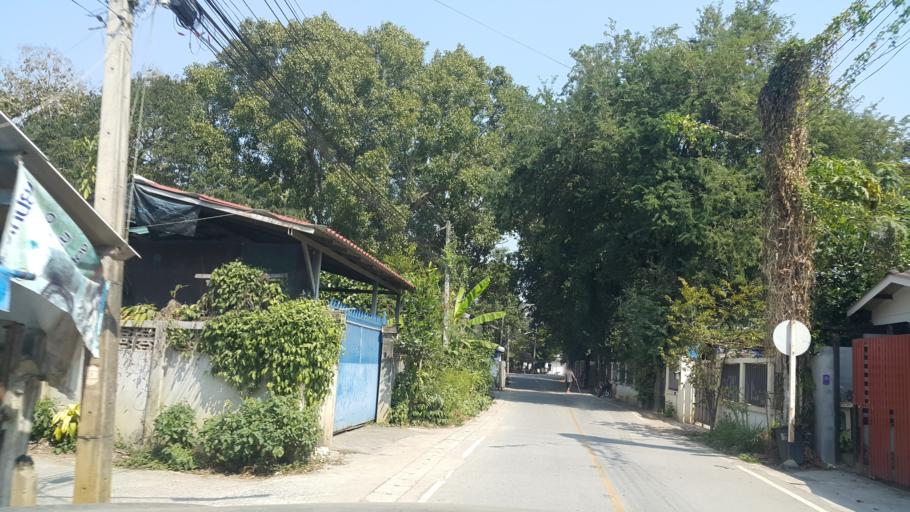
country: TH
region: Chiang Mai
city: Chiang Mai
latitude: 18.7467
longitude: 98.9952
